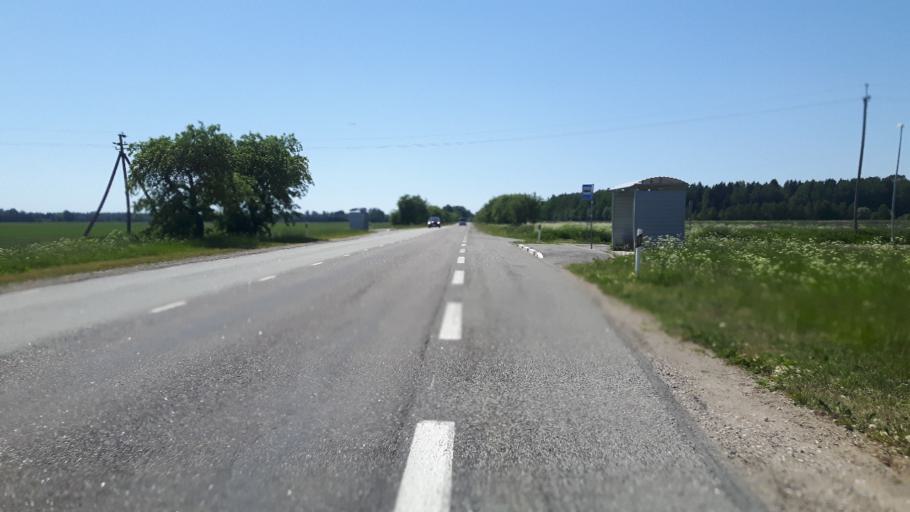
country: EE
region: Paernumaa
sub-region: Tootsi vald
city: Tootsi
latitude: 58.4751
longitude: 24.8035
